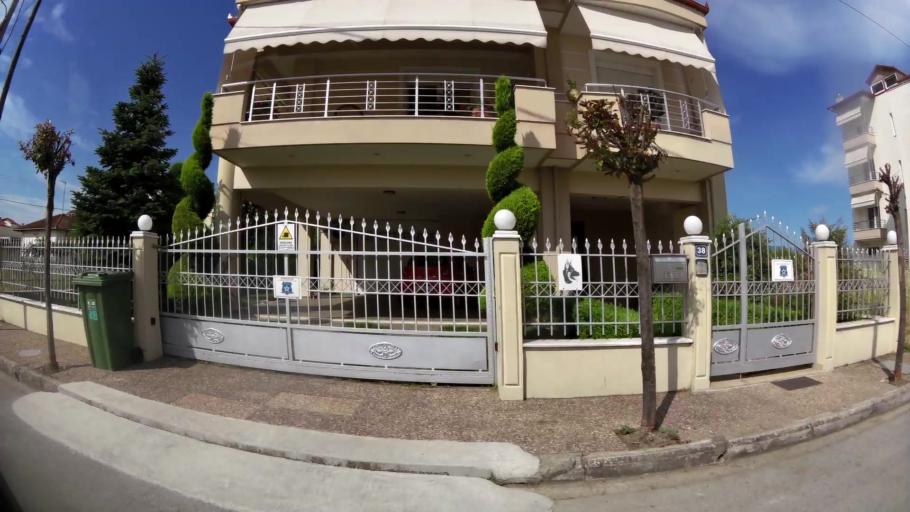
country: GR
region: Central Macedonia
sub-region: Nomos Pierias
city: Katerini
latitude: 40.2754
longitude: 22.5189
